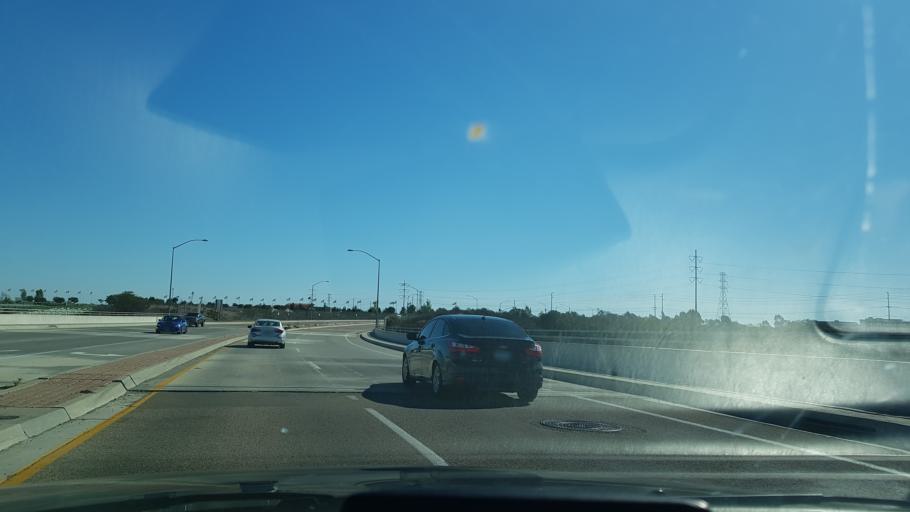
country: US
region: California
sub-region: San Diego County
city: La Jolla
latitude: 32.8761
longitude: -117.1911
